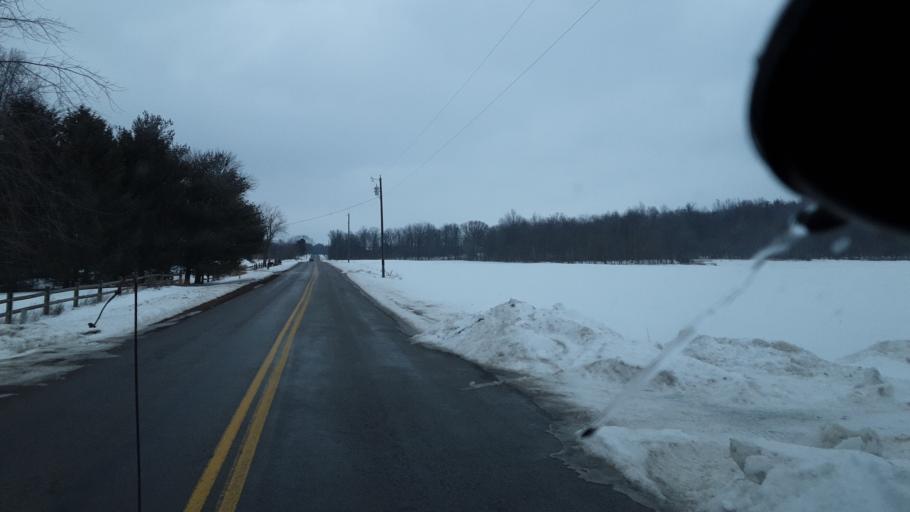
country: US
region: Ohio
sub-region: Union County
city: Marysville
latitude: 40.1794
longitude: -83.3128
